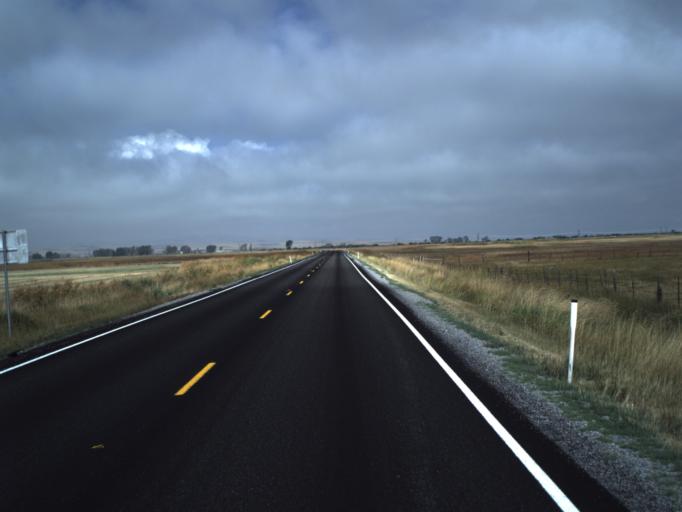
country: US
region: Utah
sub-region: Rich County
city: Randolph
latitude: 41.5052
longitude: -111.1258
